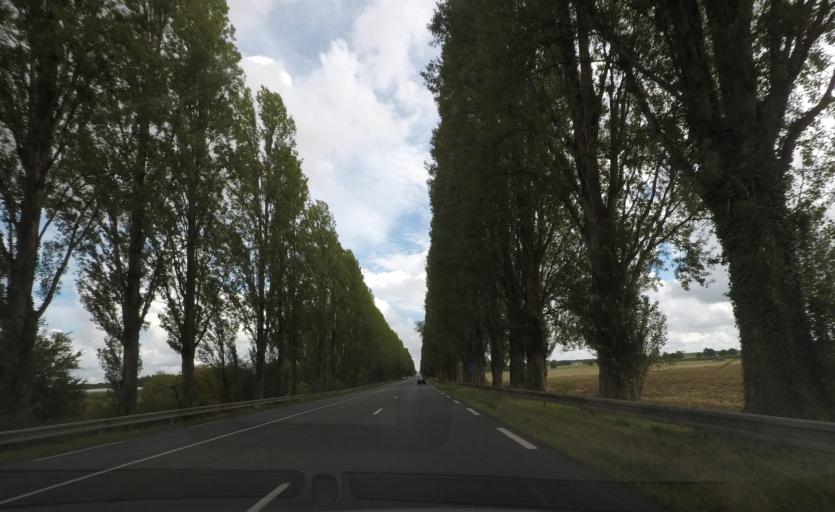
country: FR
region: Pays de la Loire
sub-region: Departement de Maine-et-Loire
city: Corze
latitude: 47.5380
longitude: -0.4072
